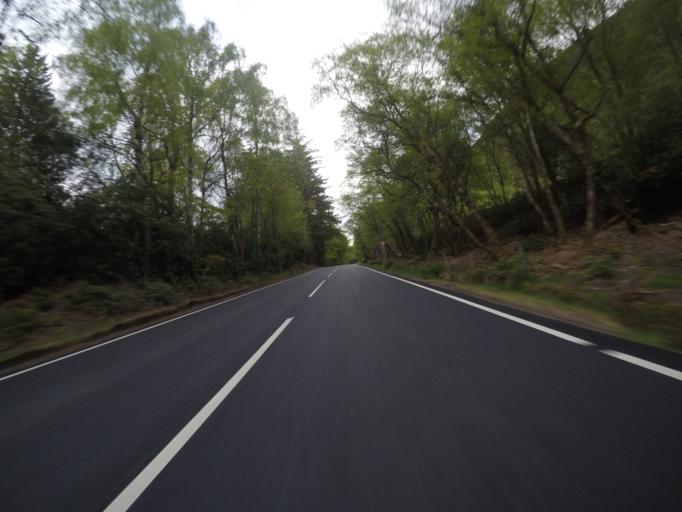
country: GB
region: Scotland
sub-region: Highland
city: Spean Bridge
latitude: 56.9547
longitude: -4.9129
